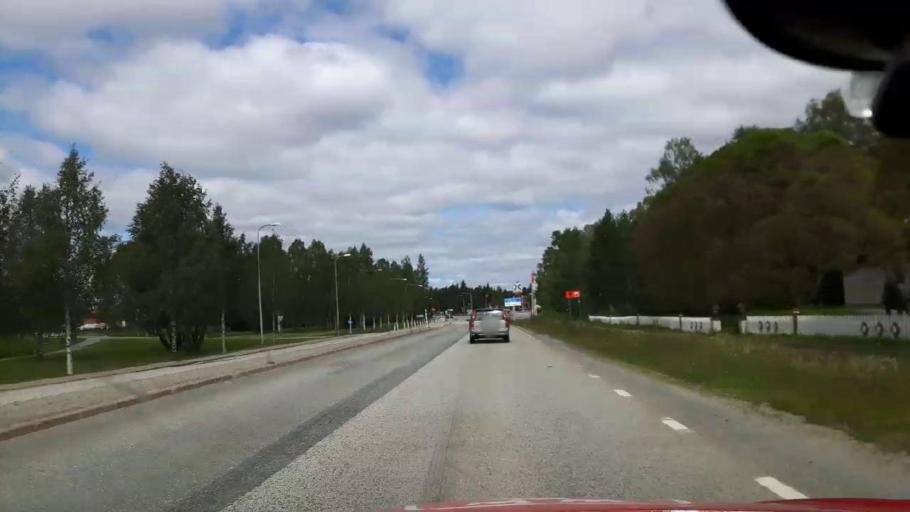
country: SE
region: Jaemtland
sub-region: Braecke Kommun
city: Braecke
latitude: 62.7546
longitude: 15.4156
